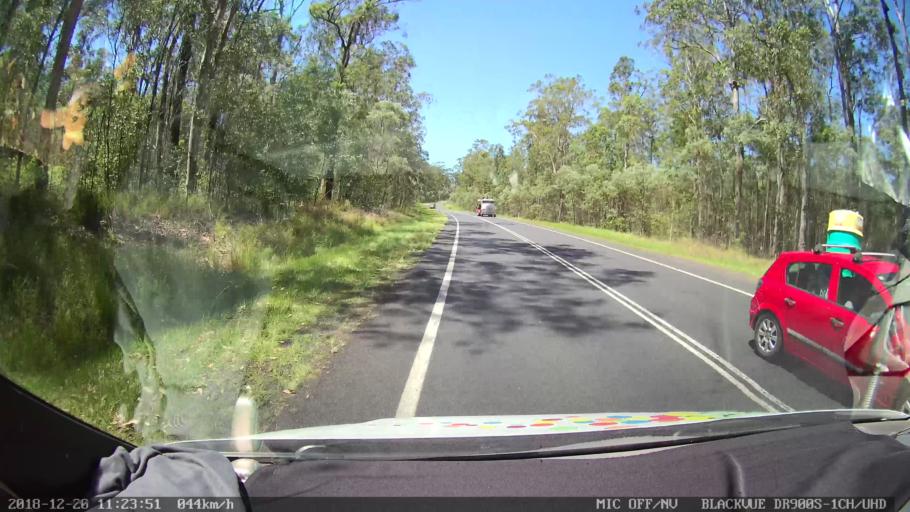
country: AU
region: New South Wales
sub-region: Richmond Valley
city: Casino
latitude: -29.0680
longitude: 153.0036
